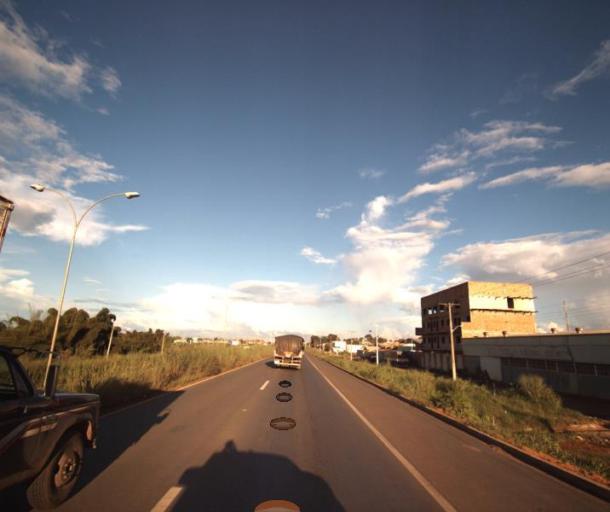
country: BR
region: Goias
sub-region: Anapolis
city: Anapolis
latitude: -16.2849
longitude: -48.9495
